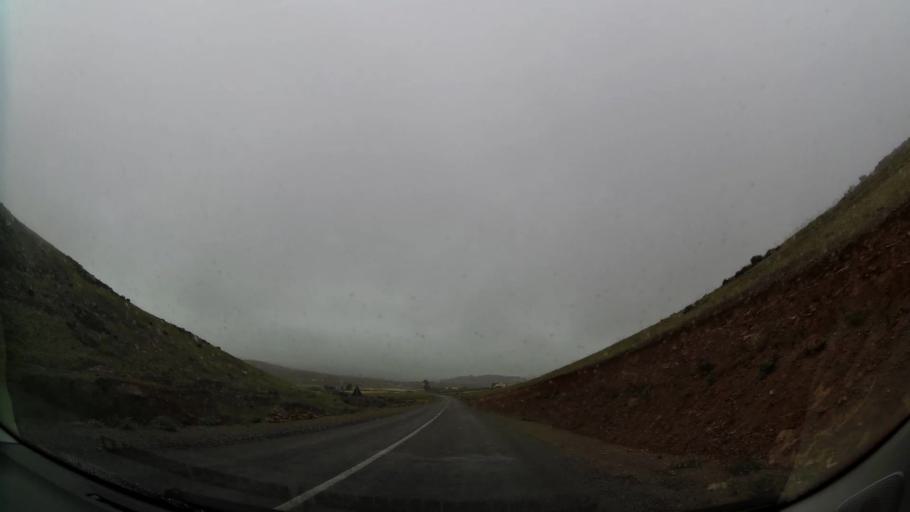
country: MA
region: Oriental
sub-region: Nador
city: Boudinar
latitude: 35.1087
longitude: -3.5688
